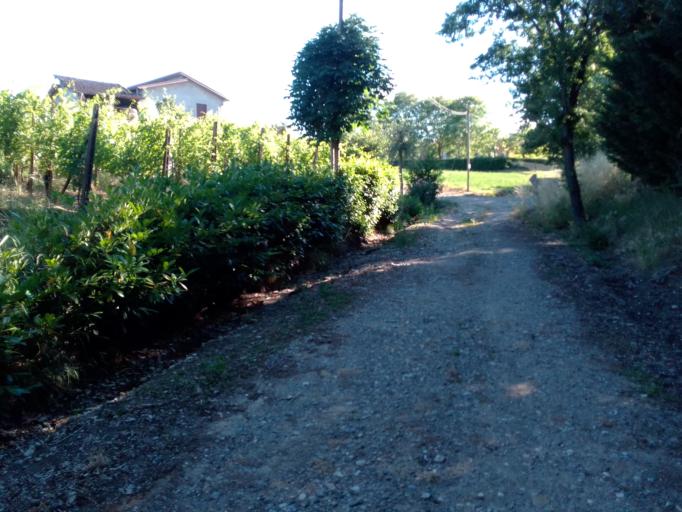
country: IT
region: Emilia-Romagna
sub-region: Provincia di Piacenza
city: Ziano Piacentino
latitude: 45.0062
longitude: 9.4165
